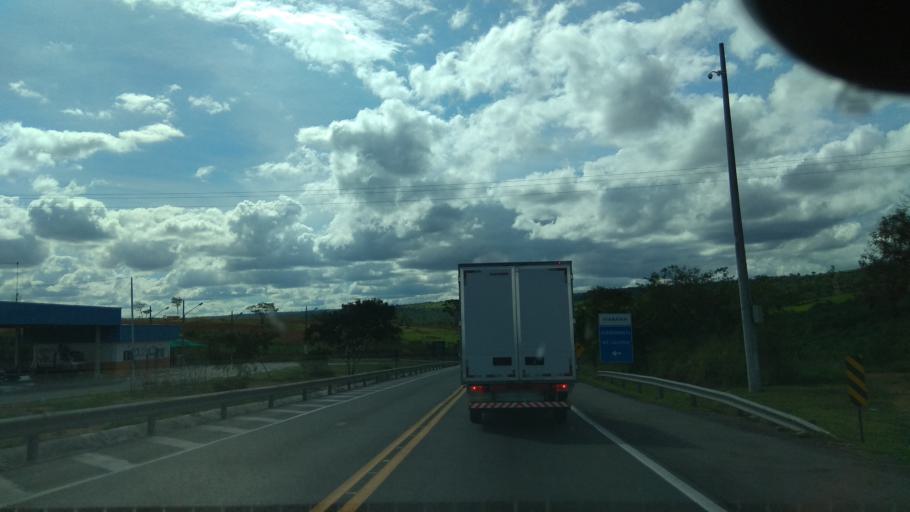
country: BR
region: Bahia
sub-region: Santa Ines
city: Santa Ines
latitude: -13.1630
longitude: -39.9993
